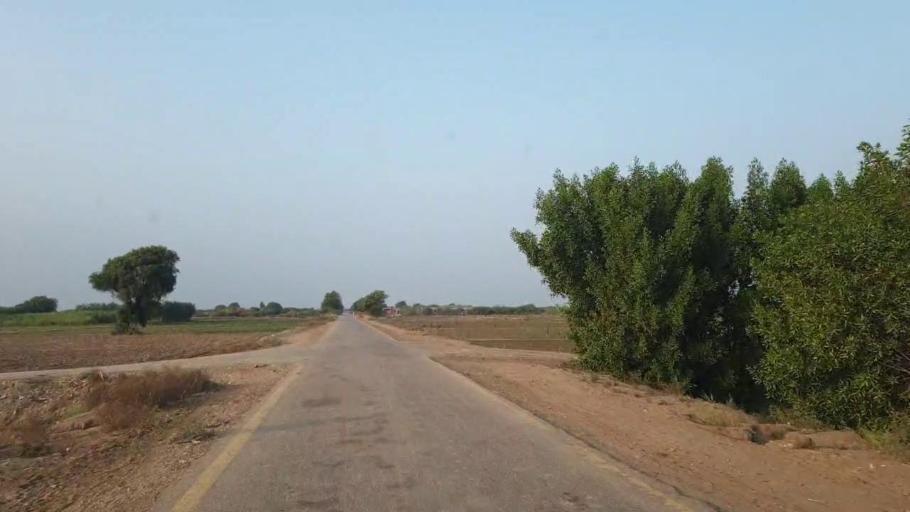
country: PK
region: Sindh
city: Tando Ghulam Ali
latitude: 25.0841
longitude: 68.9586
